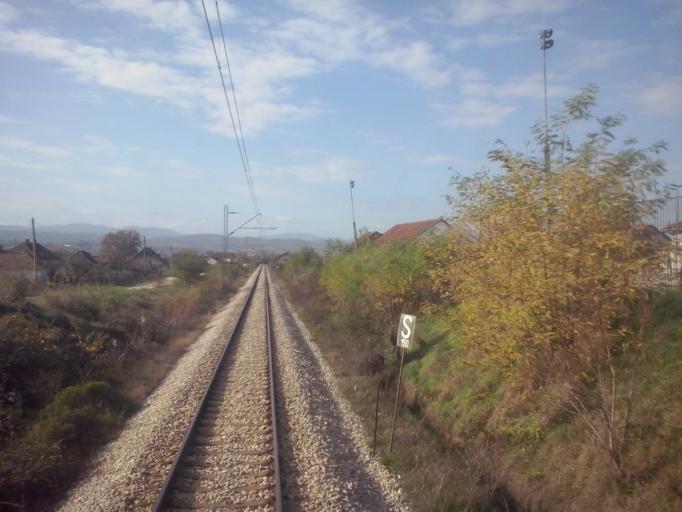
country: RS
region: Central Serbia
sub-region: Kolubarski Okrug
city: Valjevo
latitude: 44.2917
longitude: 19.9586
